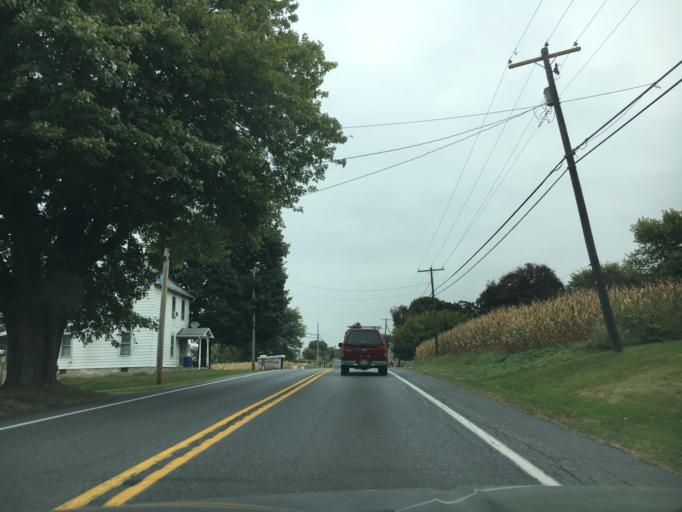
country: US
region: Pennsylvania
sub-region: Northampton County
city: North Catasauqua
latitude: 40.6990
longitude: -75.4455
